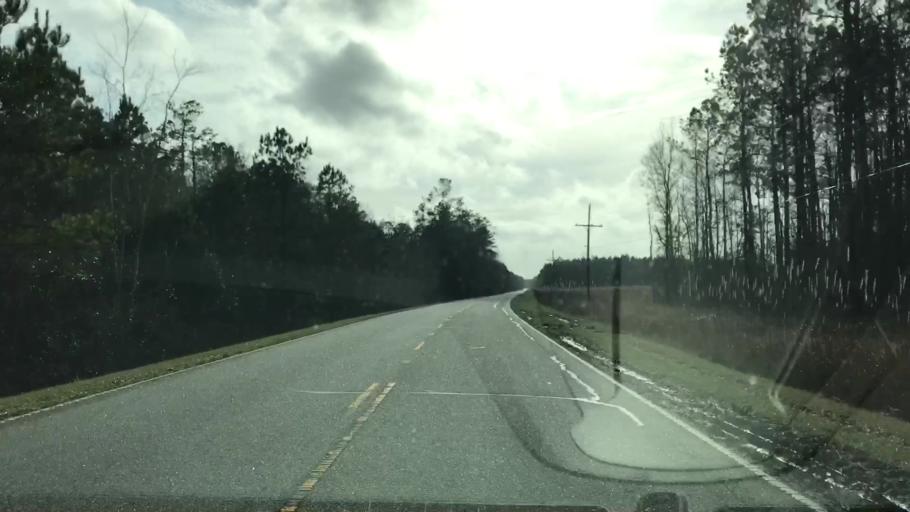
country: US
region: South Carolina
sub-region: Williamsburg County
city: Andrews
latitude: 33.4070
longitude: -79.6102
